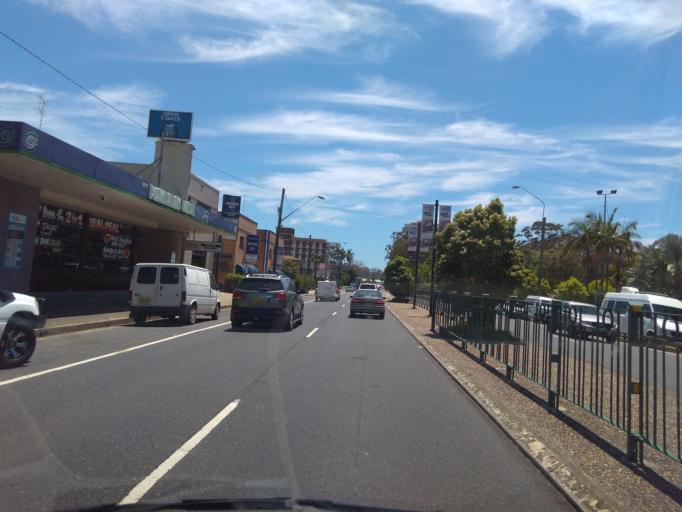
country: AU
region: New South Wales
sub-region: Coffs Harbour
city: Coffs Harbour
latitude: -30.2954
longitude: 153.1148
